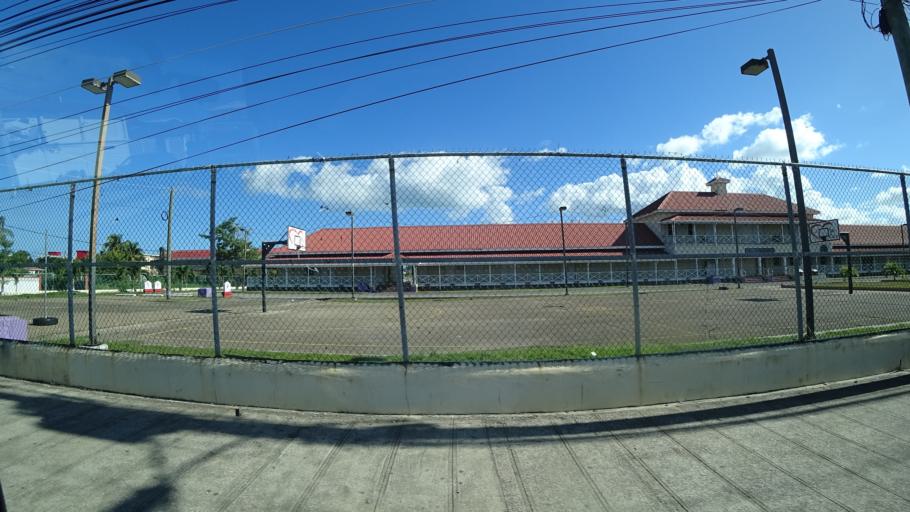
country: BZ
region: Belize
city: Belize City
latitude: 17.5031
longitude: -88.1930
